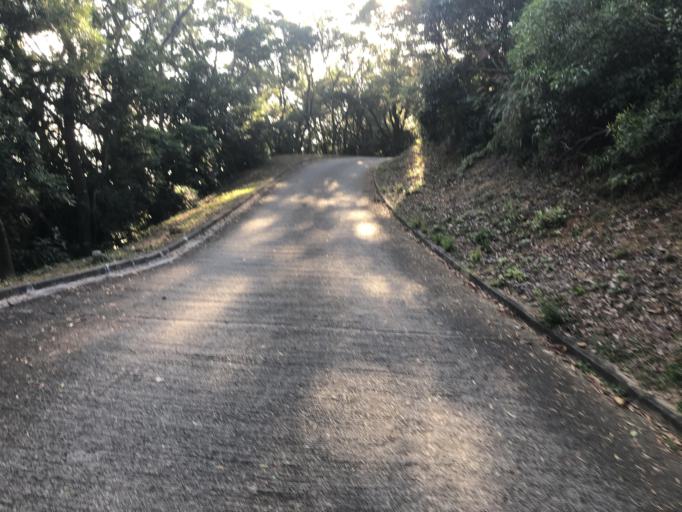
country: HK
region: Tsuen Wan
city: Tsuen Wan
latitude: 22.3977
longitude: 114.0810
